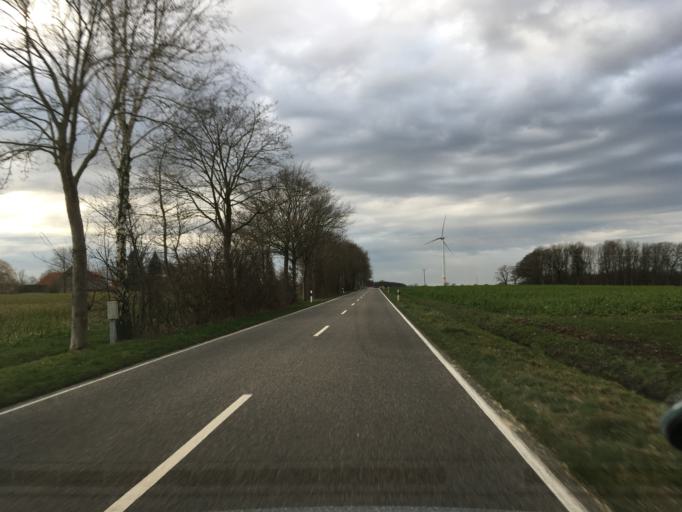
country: DE
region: North Rhine-Westphalia
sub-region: Regierungsbezirk Munster
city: Schoppingen
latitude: 52.0738
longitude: 7.1995
